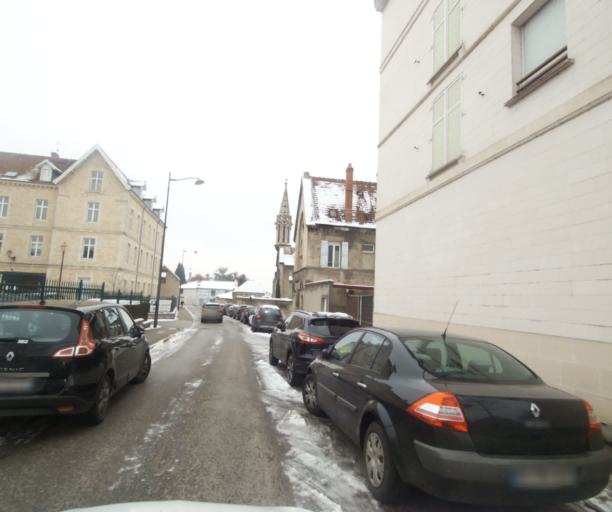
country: FR
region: Champagne-Ardenne
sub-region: Departement de la Haute-Marne
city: Saint-Dizier
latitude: 48.6363
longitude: 4.9470
